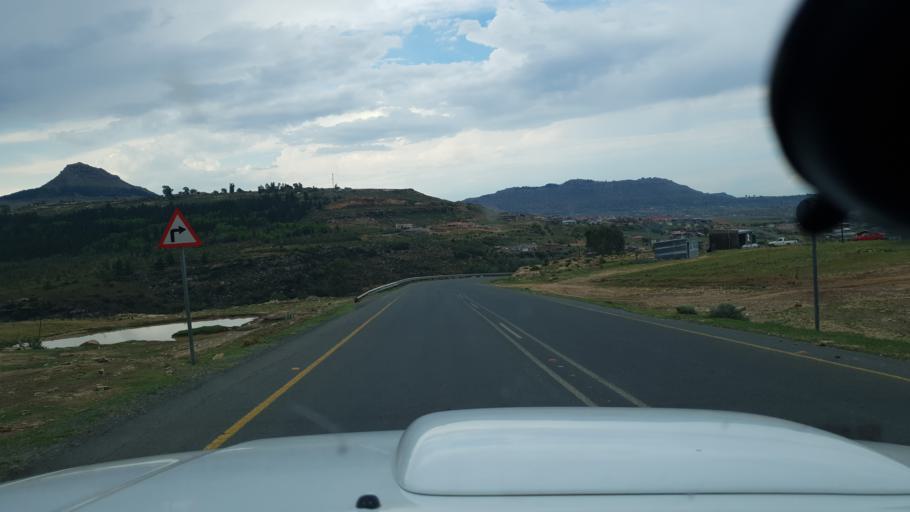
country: LS
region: Maseru
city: Maseru
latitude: -29.4061
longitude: 27.4701
